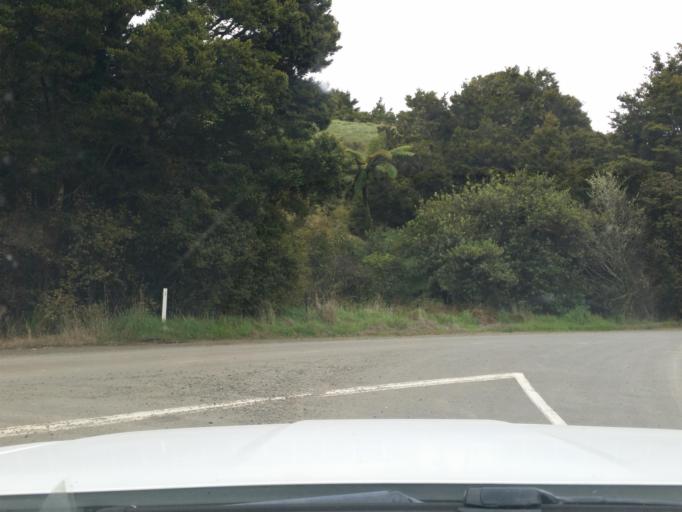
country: NZ
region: Northland
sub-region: Kaipara District
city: Dargaville
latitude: -35.7062
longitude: 173.5982
